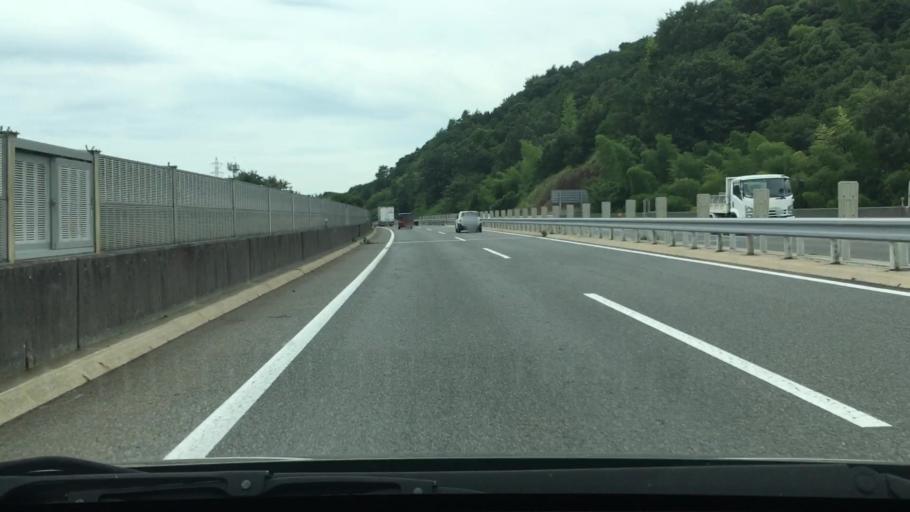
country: JP
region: Hiroshima
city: Ono-hara
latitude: 34.2850
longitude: 132.2622
